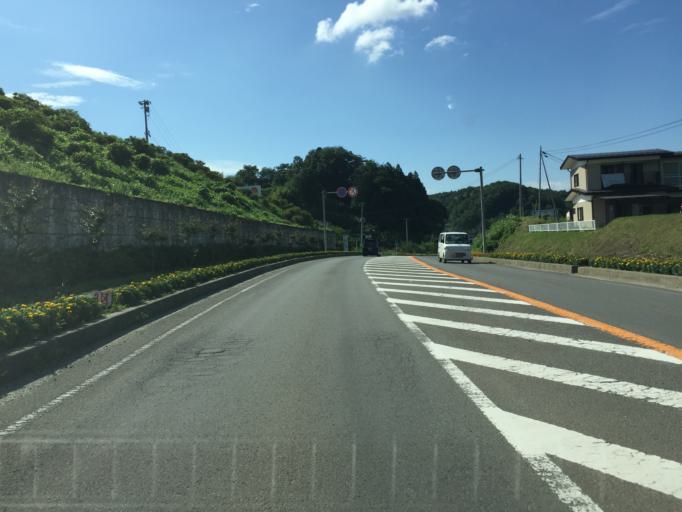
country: JP
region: Fukushima
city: Fukushima-shi
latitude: 37.6639
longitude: 140.5918
